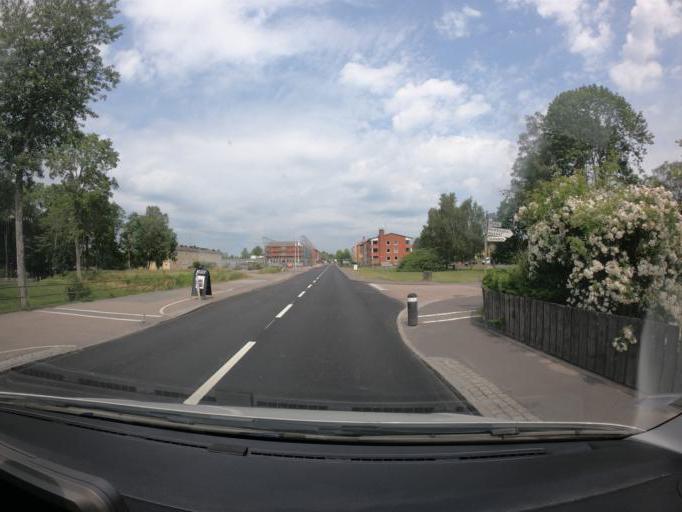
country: SE
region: Skane
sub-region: Hassleholms Kommun
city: Bjarnum
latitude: 56.2884
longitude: 13.7119
